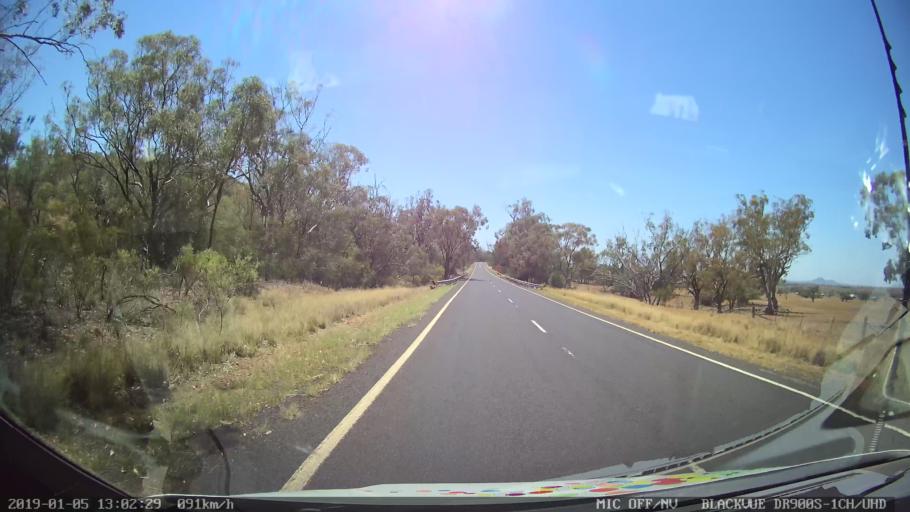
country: AU
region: New South Wales
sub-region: Narrabri
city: Boggabri
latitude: -31.1147
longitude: 149.8124
